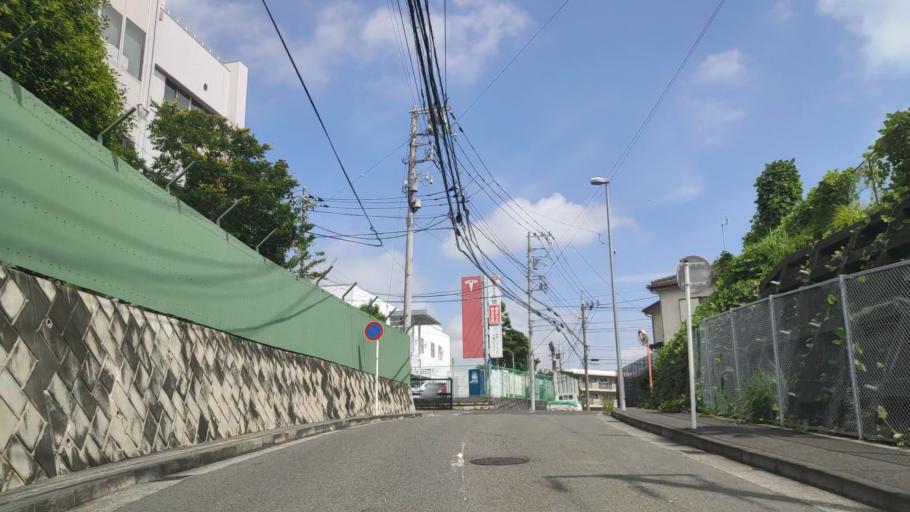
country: JP
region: Kanagawa
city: Minami-rinkan
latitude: 35.4252
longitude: 139.5373
